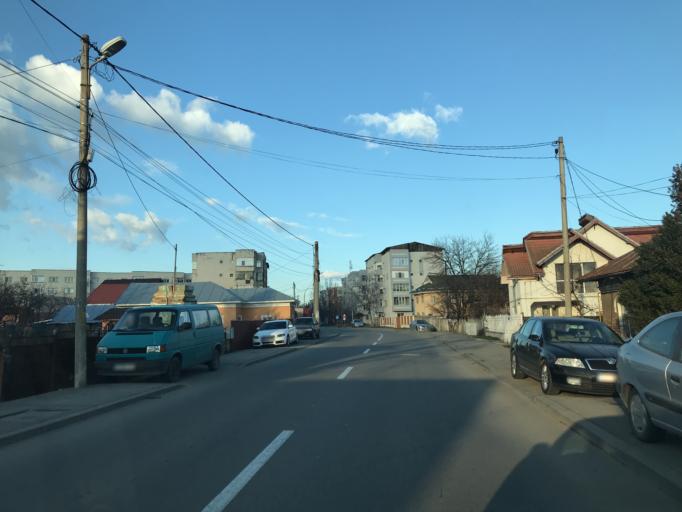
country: RO
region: Olt
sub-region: Municipiul Slatina
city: Slatina
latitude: 44.4157
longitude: 24.3799
